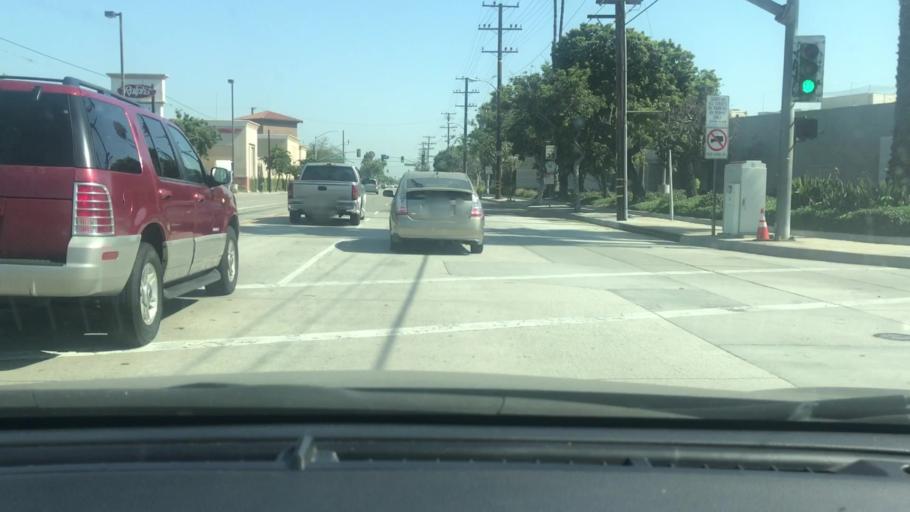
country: US
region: California
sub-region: Los Angeles County
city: Gardena
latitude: 33.8859
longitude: -118.3178
